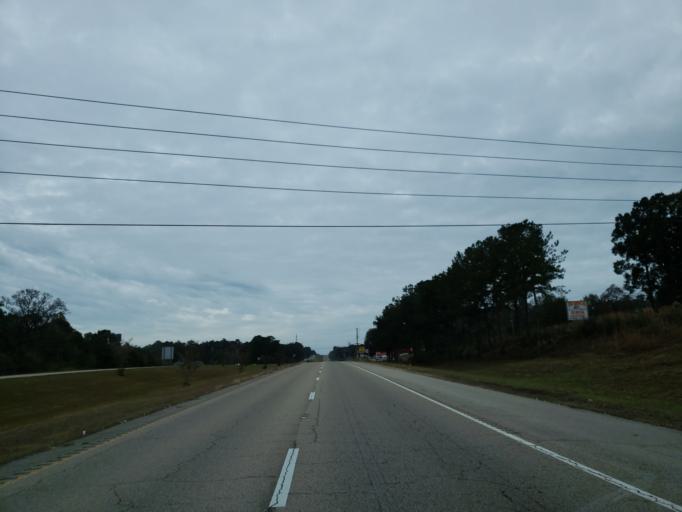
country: US
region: Mississippi
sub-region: Forrest County
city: Hattiesburg
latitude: 31.2380
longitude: -89.2732
